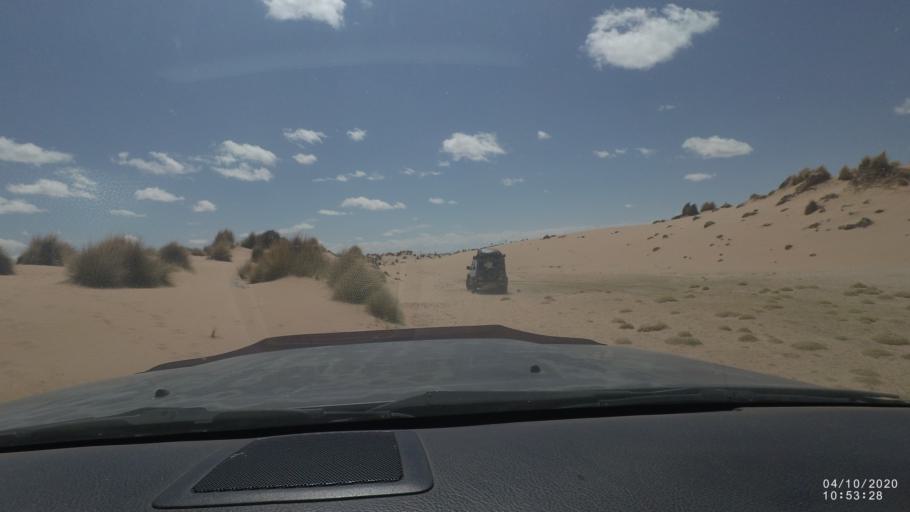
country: BO
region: Oruro
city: Poopo
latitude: -18.7018
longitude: -67.4685
